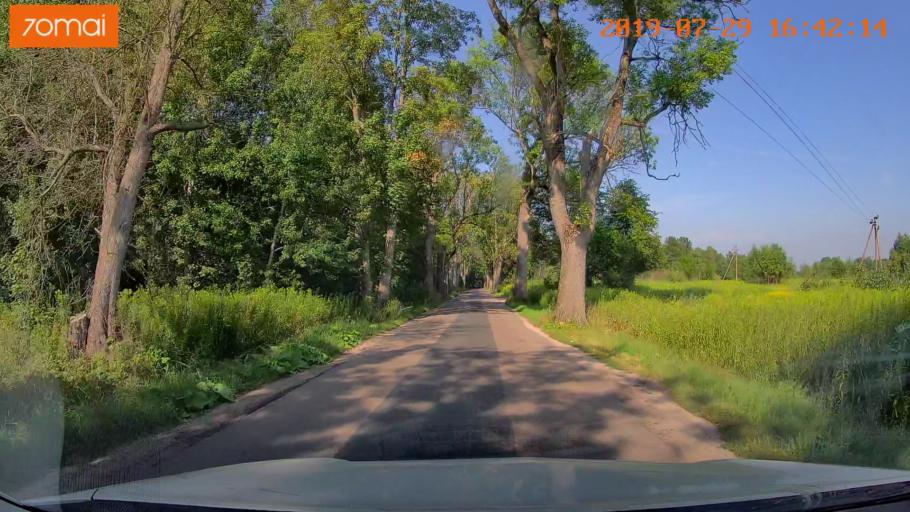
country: RU
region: Kaliningrad
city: Primorsk
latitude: 54.7416
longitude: 20.0709
